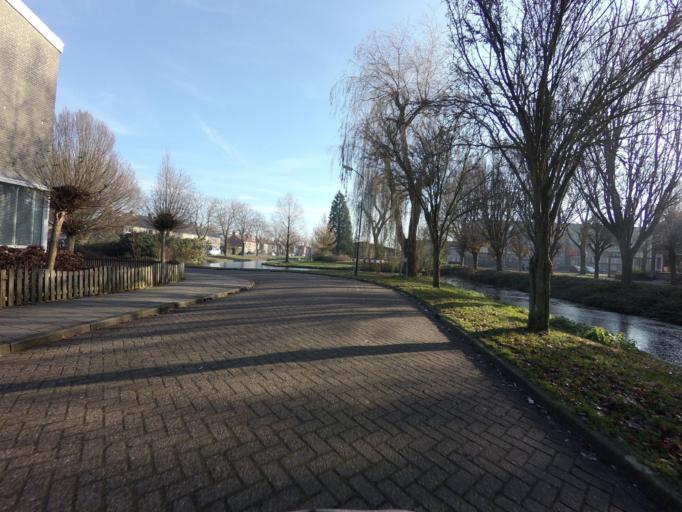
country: NL
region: Utrecht
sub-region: Gemeente De Ronde Venen
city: Mijdrecht
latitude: 52.2050
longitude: 4.8556
